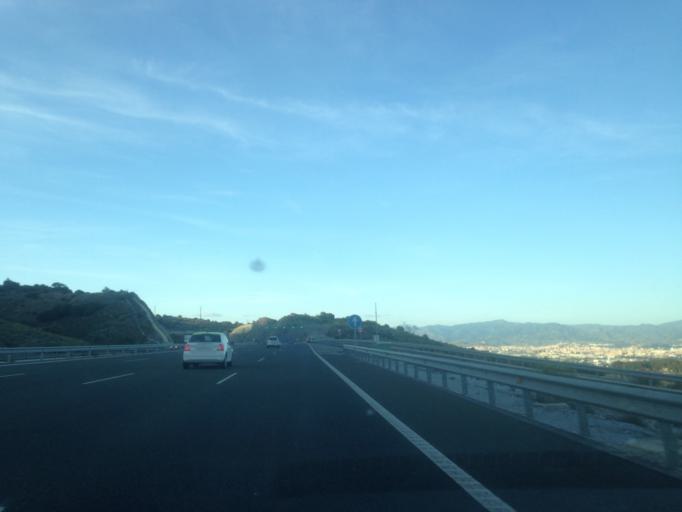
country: ES
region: Andalusia
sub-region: Provincia de Malaga
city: Torremolinos
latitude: 36.6429
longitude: -4.5136
